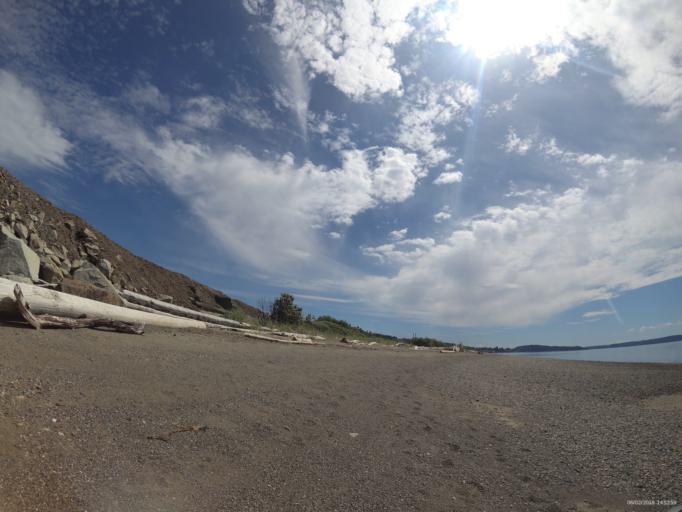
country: US
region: Washington
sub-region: Pierce County
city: Steilacoom
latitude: 47.1924
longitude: -122.5825
